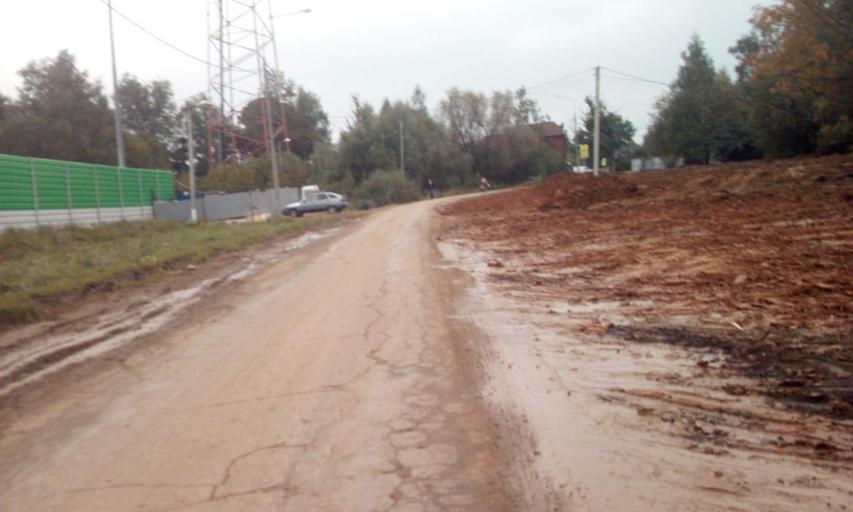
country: RU
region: Moskovskaya
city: Zhavoronki
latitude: 55.6428
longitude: 37.1050
